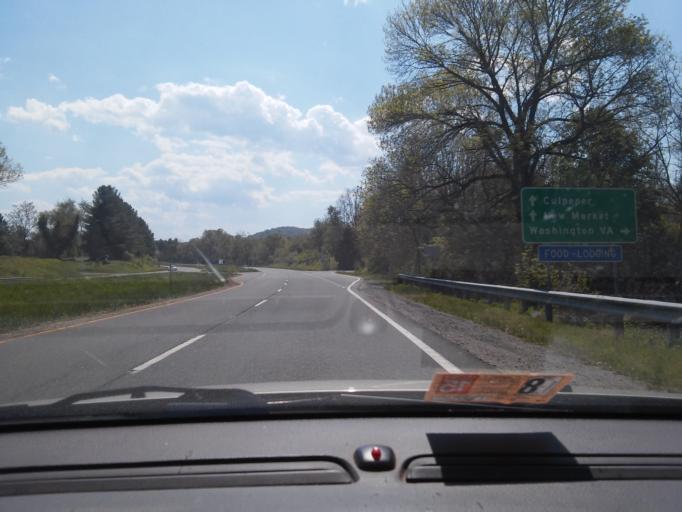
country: US
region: Virginia
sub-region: Rappahannock County
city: Washington
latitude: 38.7124
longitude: -78.1519
